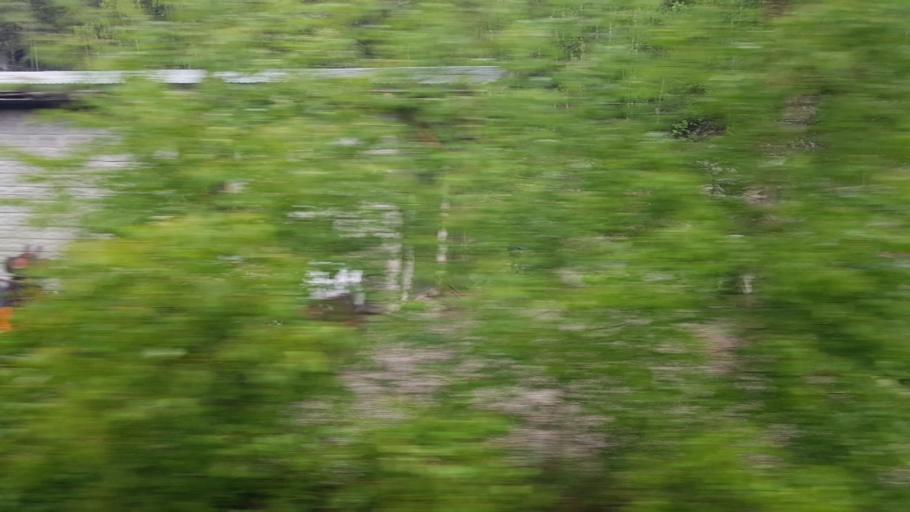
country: NO
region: Oppland
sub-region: Ringebu
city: Ringebu
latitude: 61.5338
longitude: 10.1318
